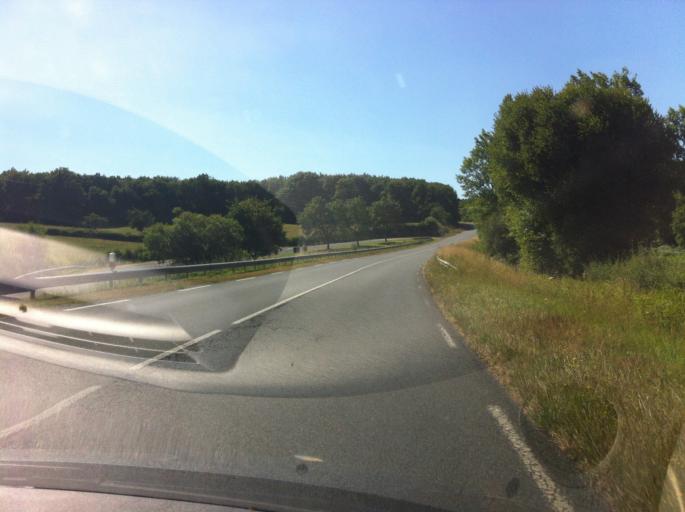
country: FR
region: Auvergne
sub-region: Departement de l'Allier
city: Chantelle
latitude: 46.3196
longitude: 3.1027
